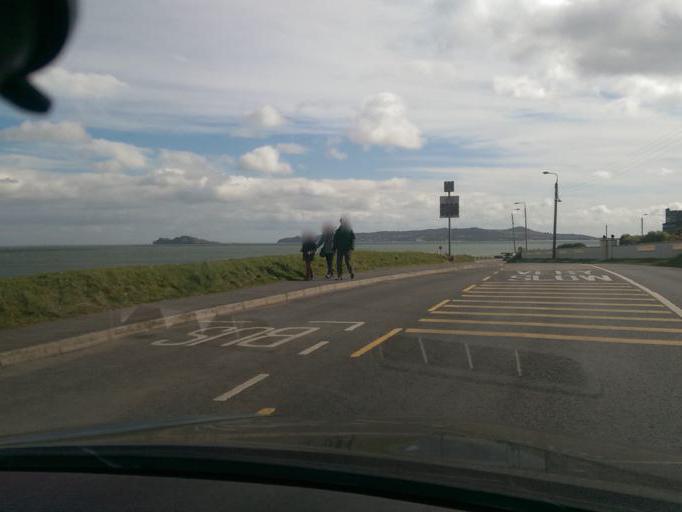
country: IE
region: Leinster
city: Portmarnock
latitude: 53.4380
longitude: -6.1228
